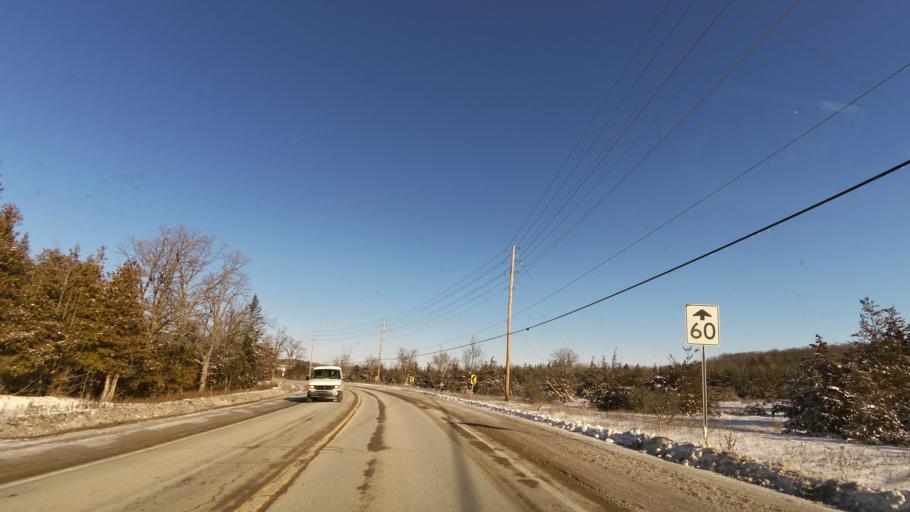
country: CA
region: Ontario
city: Quinte West
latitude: 44.2799
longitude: -77.8084
